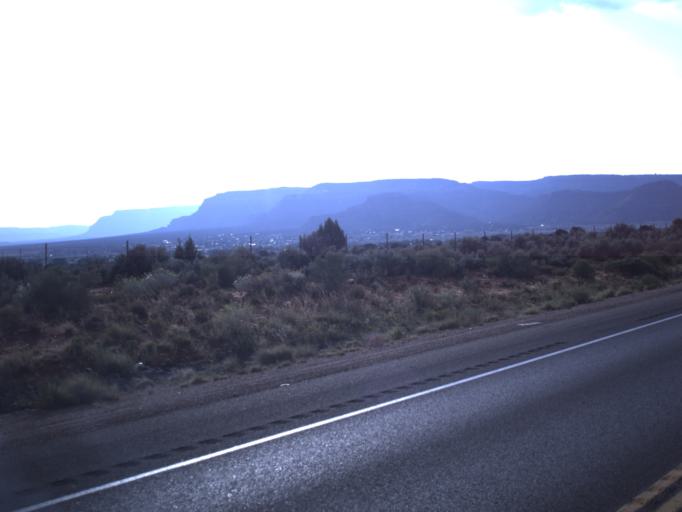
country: US
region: Utah
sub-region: Kane County
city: Kanab
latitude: 37.0323
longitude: -112.4945
